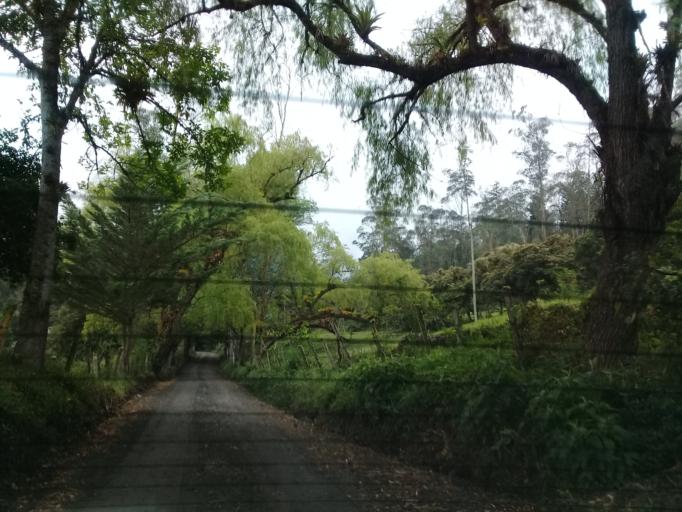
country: CO
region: Cundinamarca
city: Caqueza
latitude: 4.3926
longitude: -73.9803
